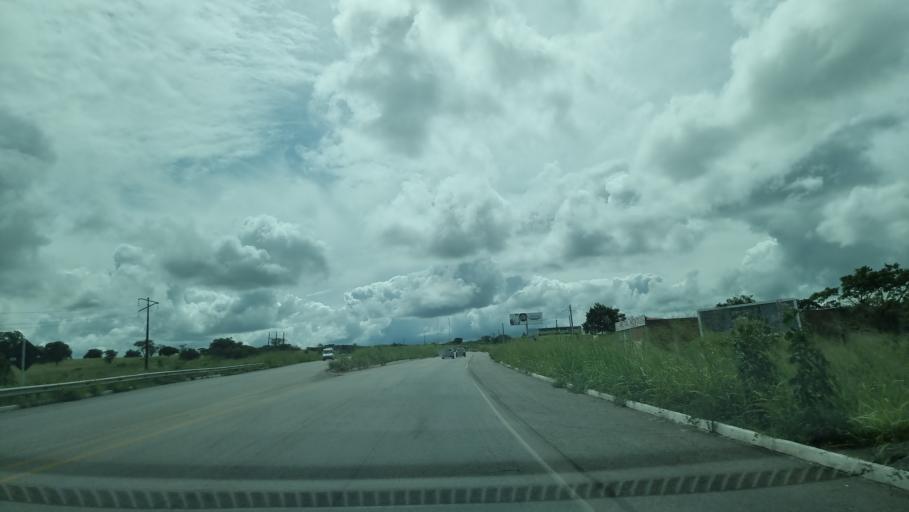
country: BR
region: Pernambuco
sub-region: Caruaru
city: Caruaru
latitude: -8.3324
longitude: -35.9819
